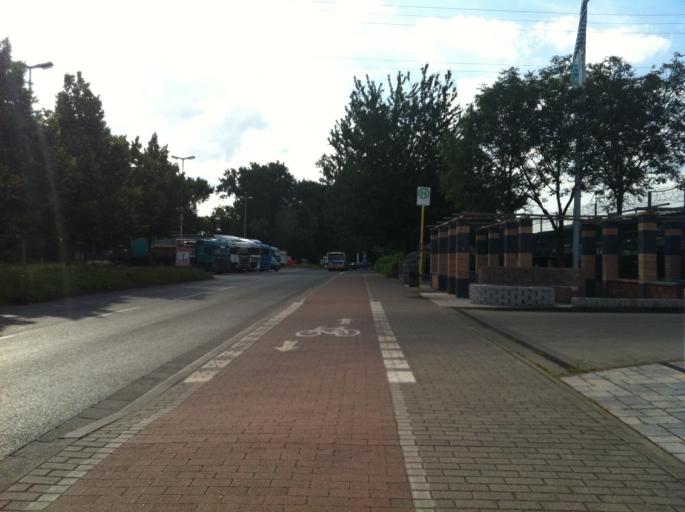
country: DE
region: Rheinland-Pfalz
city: Budenheim
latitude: 50.0289
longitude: 8.2210
